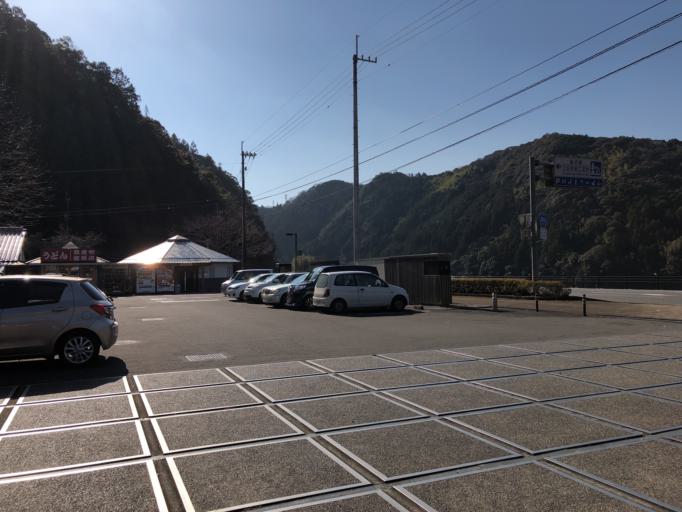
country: JP
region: Kochi
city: Ino
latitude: 33.5736
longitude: 133.3661
